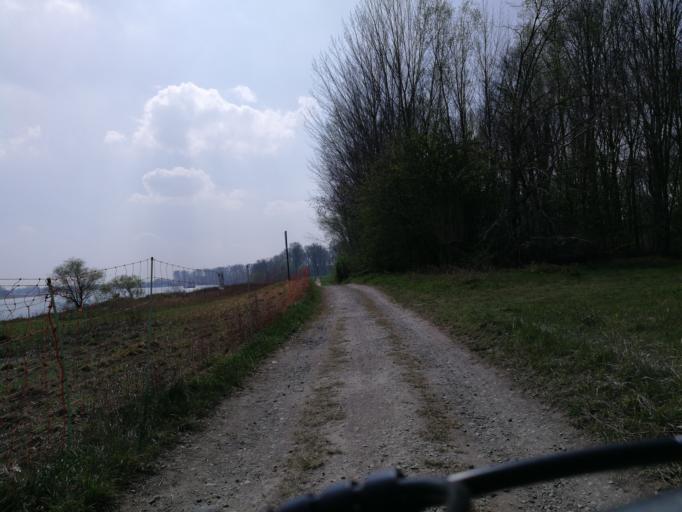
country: DE
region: North Rhine-Westphalia
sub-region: Regierungsbezirk Dusseldorf
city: Dormagen
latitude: 51.1500
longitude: 6.8513
